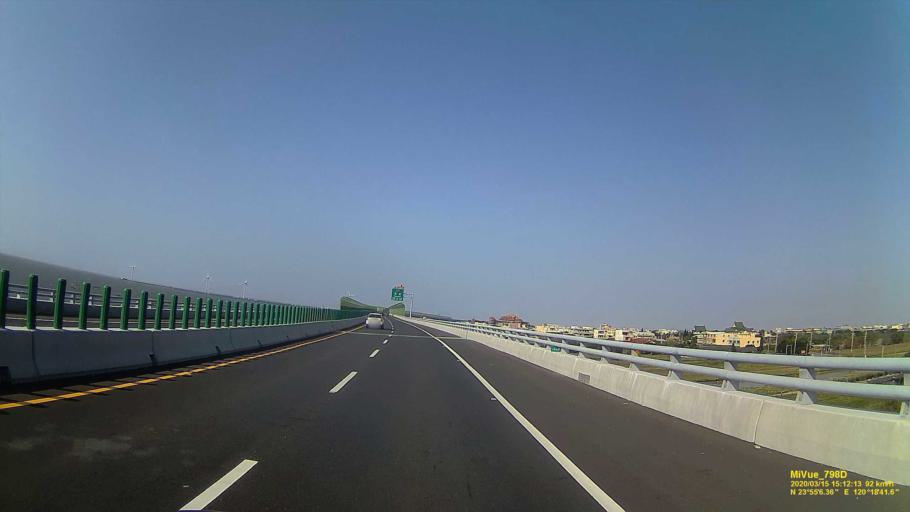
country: TW
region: Taiwan
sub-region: Changhua
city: Chang-hua
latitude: 23.9189
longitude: 120.3116
